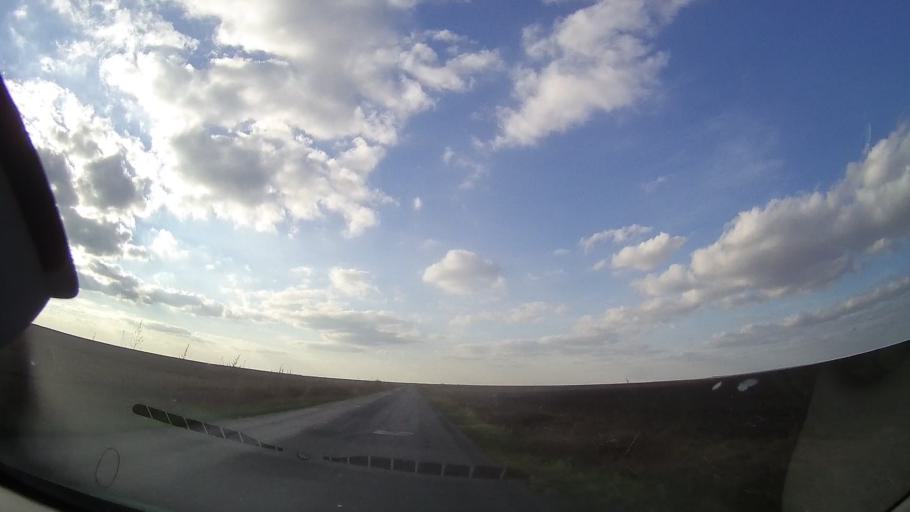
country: RO
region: Constanta
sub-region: Comuna Negru Voda
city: Negru Voda
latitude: 43.8211
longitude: 28.1673
